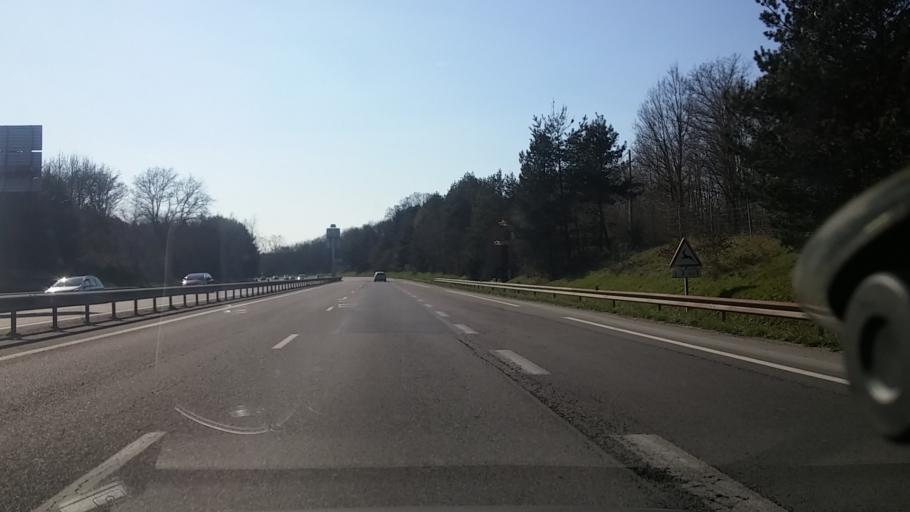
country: FR
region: Centre
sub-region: Departement du Cher
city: Vierzon
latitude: 47.2442
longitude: 2.0549
